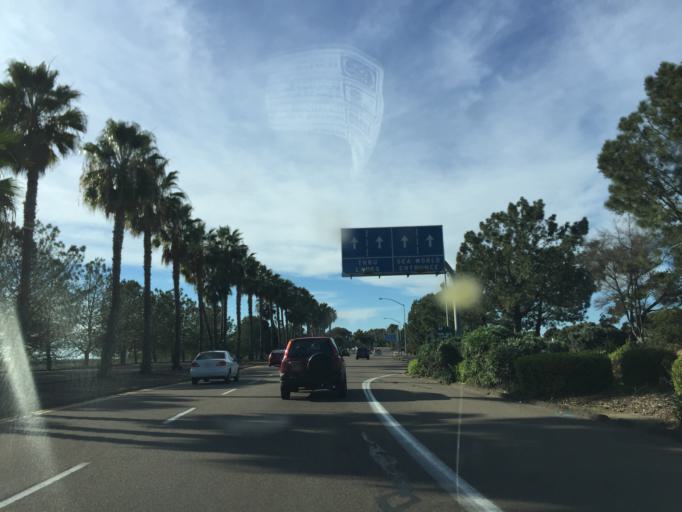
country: US
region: California
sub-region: San Diego County
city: San Diego
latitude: 32.7611
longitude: -117.2214
